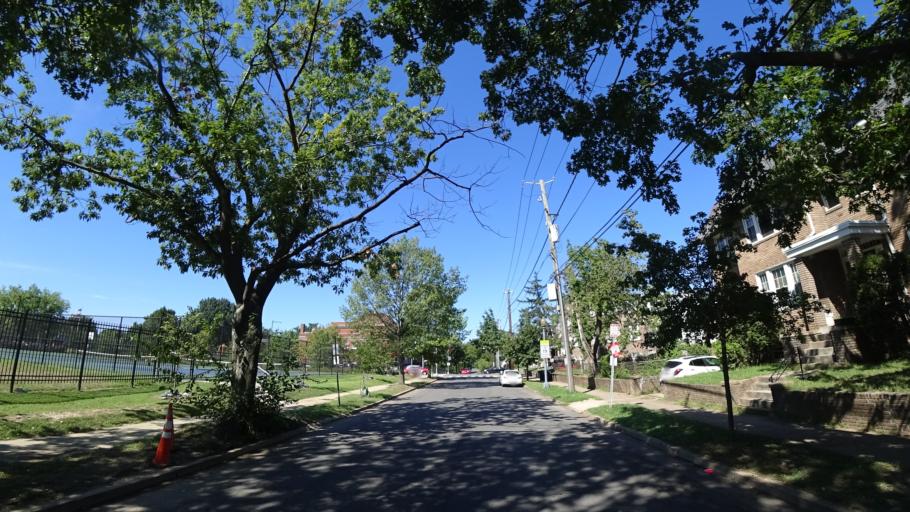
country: US
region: Maryland
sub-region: Montgomery County
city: Takoma Park
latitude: 38.9451
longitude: -77.0289
